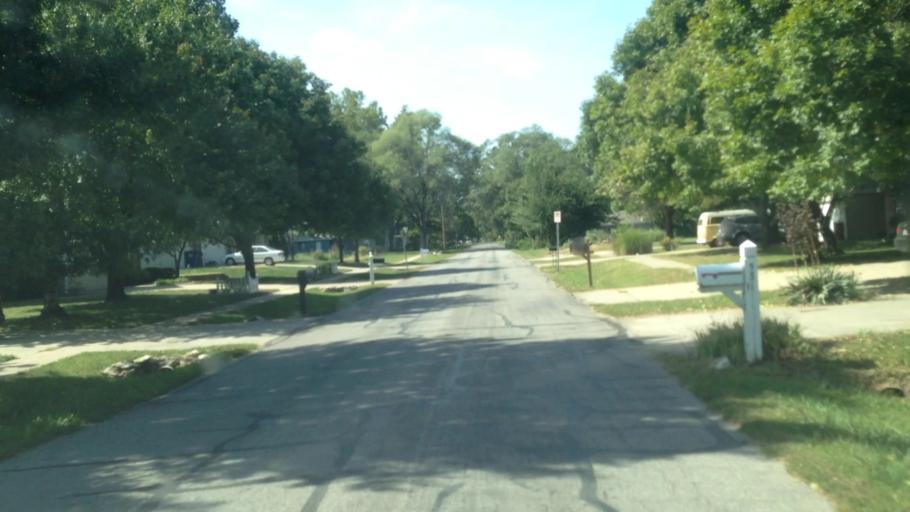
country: US
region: Kansas
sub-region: Douglas County
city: Lawrence
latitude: 38.9824
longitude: -95.2267
